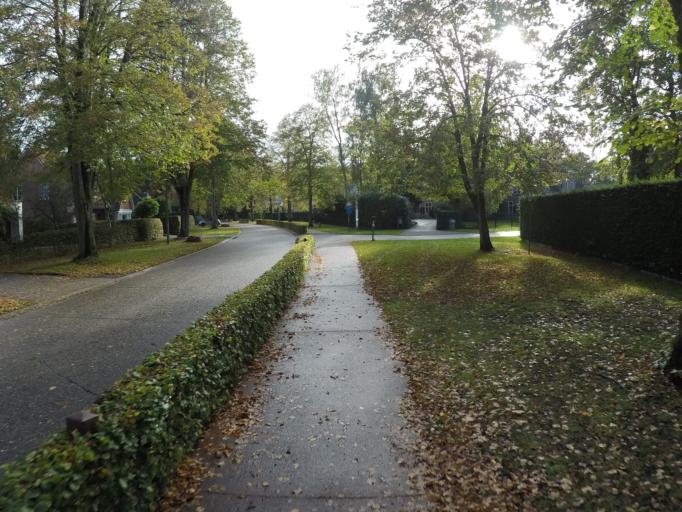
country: BE
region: Flanders
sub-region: Provincie Antwerpen
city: Schilde
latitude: 51.2297
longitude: 4.5542
